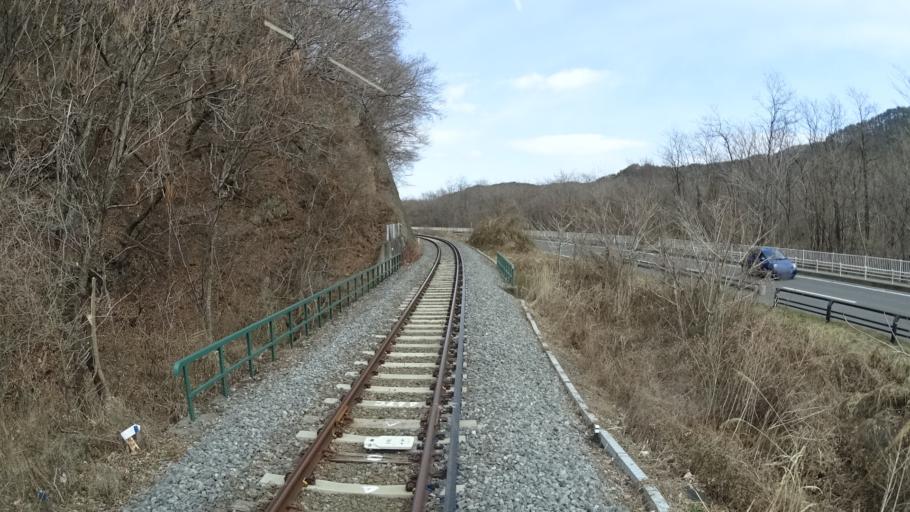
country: JP
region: Iwate
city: Yamada
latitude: 39.5516
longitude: 141.9397
